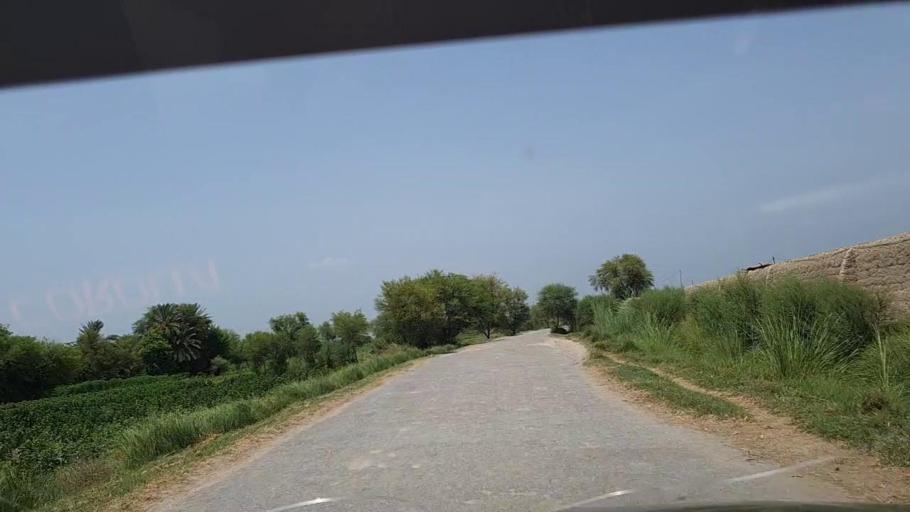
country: PK
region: Sindh
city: Khanpur
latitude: 27.8004
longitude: 69.4511
